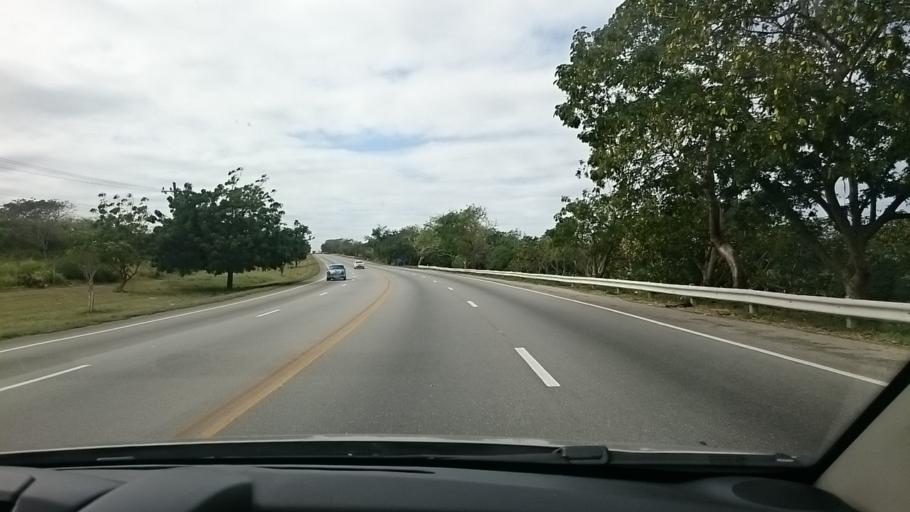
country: CU
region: La Habana
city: Alamar
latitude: 23.1675
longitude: -82.2569
